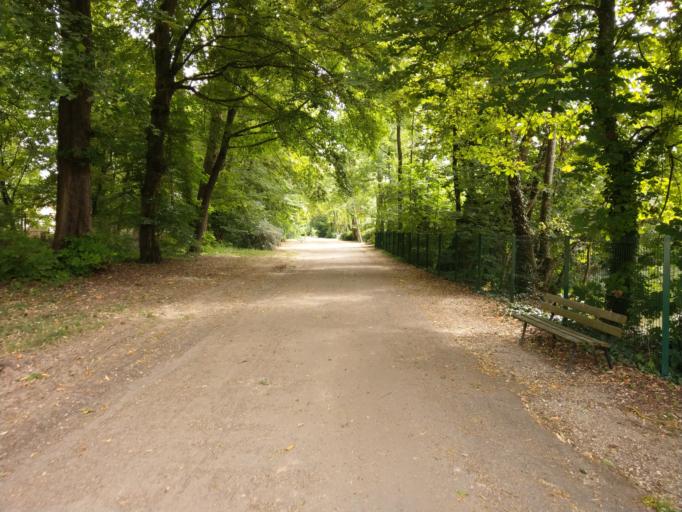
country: FR
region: Bourgogne
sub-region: Departement de la Cote-d'Or
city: Dijon
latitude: 47.3186
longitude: 5.0176
